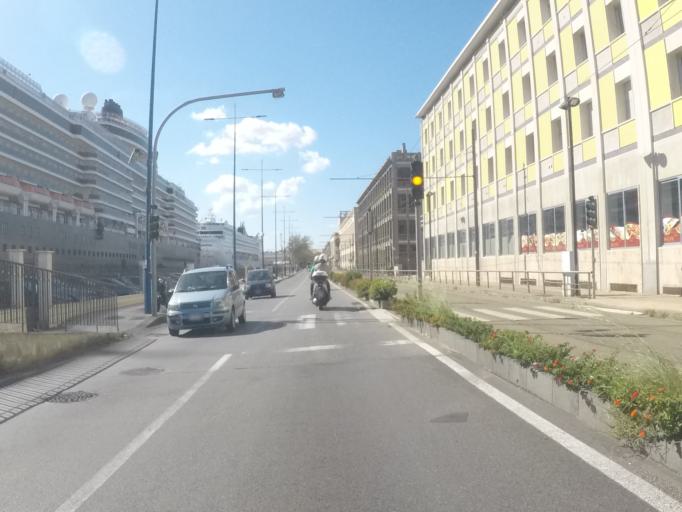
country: IT
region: Sicily
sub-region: Messina
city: Messina
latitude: 38.1963
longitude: 15.5576
